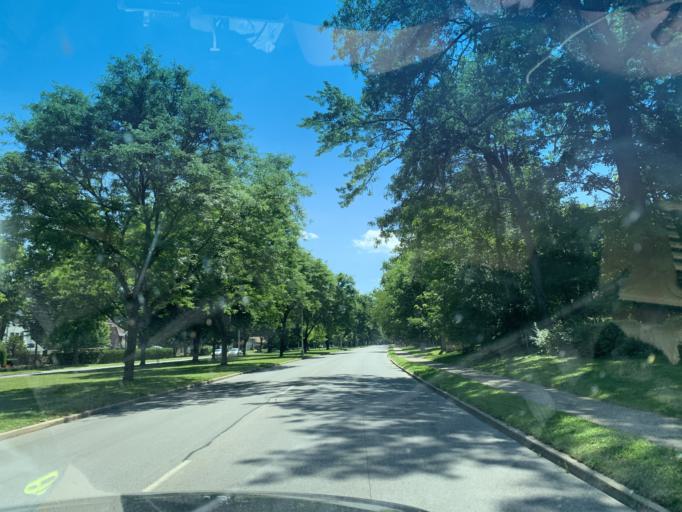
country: US
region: New York
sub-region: Oneida County
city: Utica
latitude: 43.0772
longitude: -75.2261
